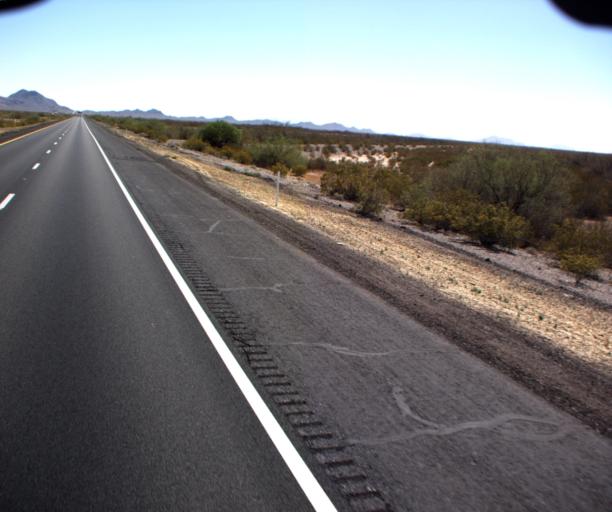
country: US
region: Arizona
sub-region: La Paz County
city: Salome
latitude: 33.6230
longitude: -113.7157
